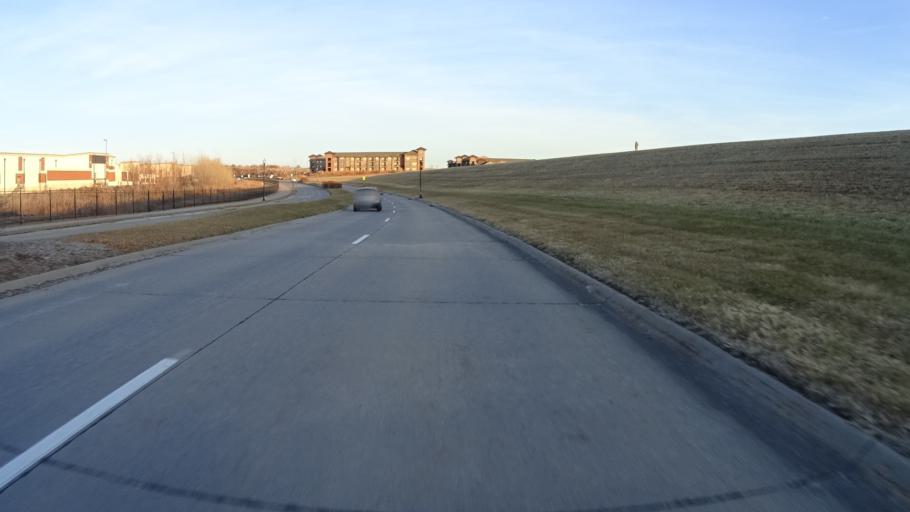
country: US
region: Nebraska
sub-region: Sarpy County
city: Papillion
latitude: 41.1318
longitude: -96.0306
